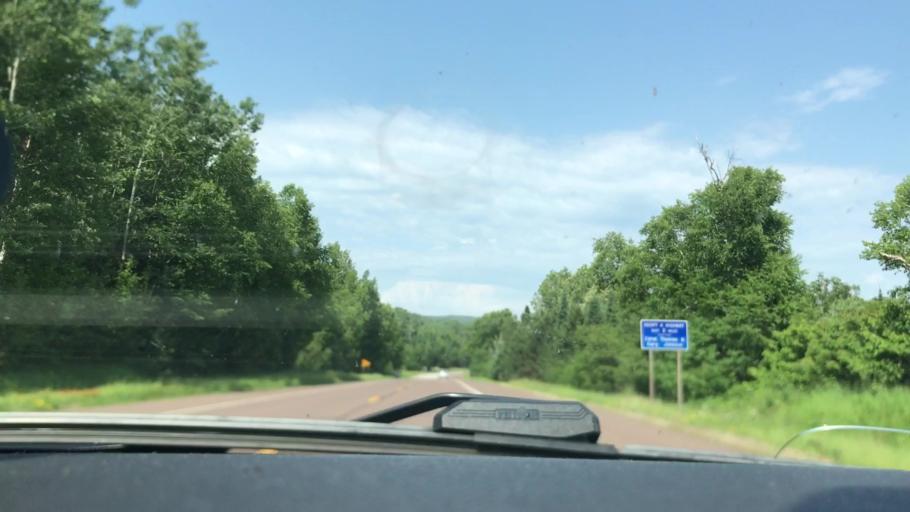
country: US
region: Minnesota
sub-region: Cook County
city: Grand Marais
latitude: 47.7809
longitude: -90.1875
